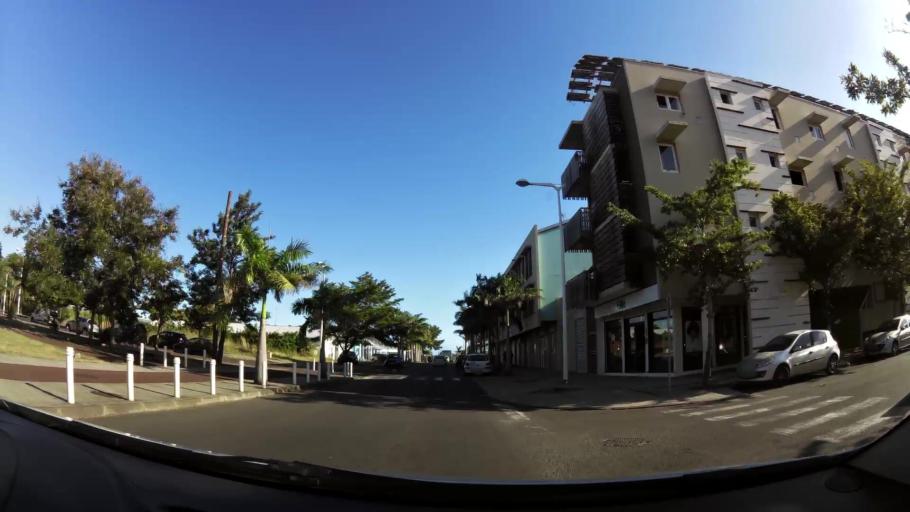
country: RE
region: Reunion
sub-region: Reunion
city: Saint-Louis
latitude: -21.2893
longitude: 55.4044
